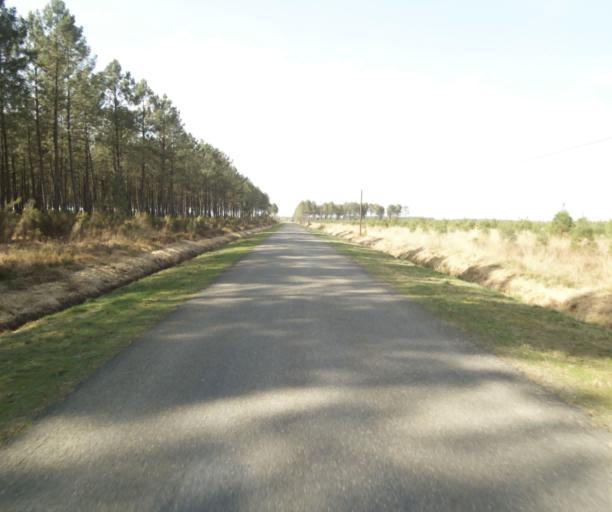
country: FR
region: Aquitaine
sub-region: Departement des Landes
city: Roquefort
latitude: 44.1832
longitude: -0.2253
